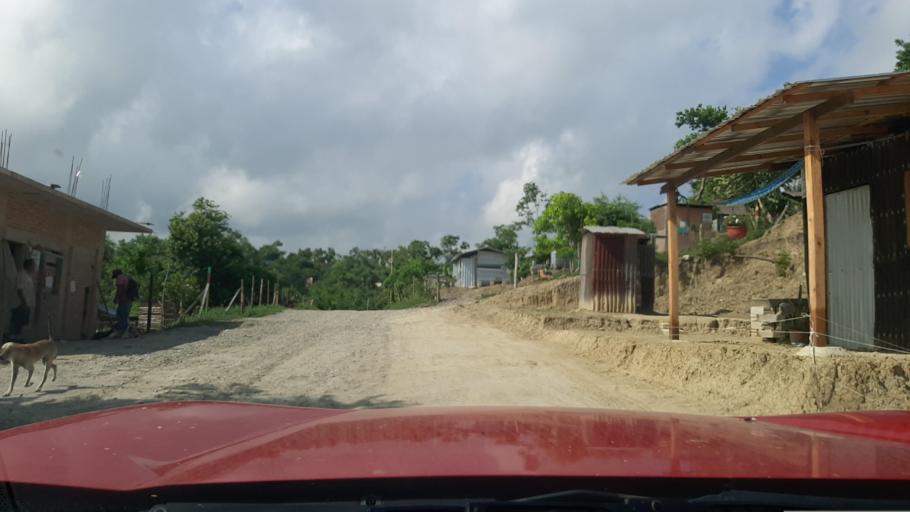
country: MX
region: Veracruz
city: Coatzintla
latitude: 20.5057
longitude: -97.4597
